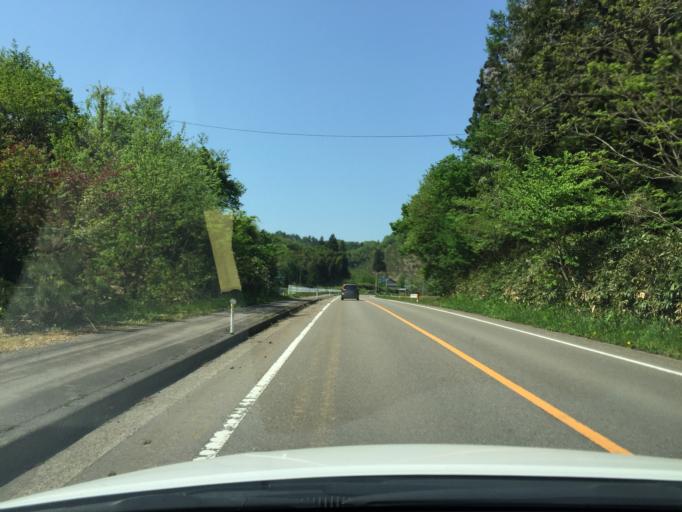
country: JP
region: Niigata
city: Muramatsu
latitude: 37.6453
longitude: 139.1263
